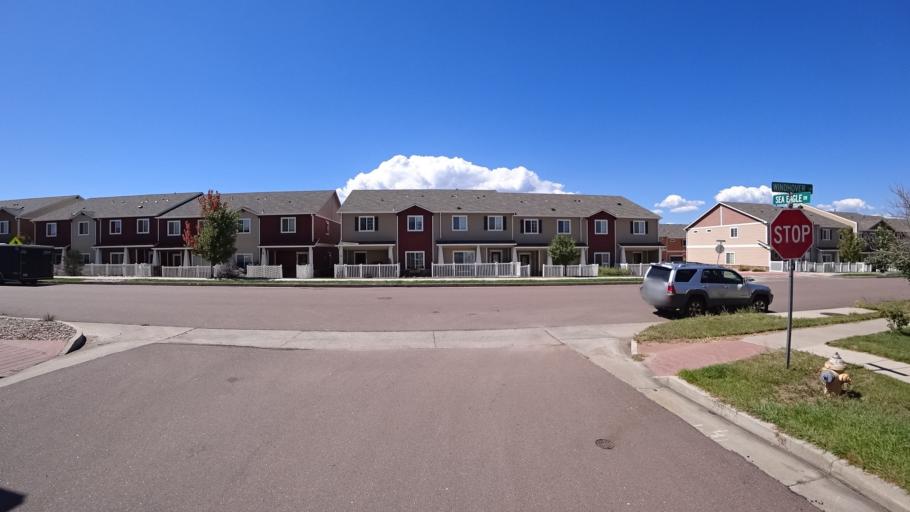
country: US
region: Colorado
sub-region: El Paso County
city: Stratmoor
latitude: 38.7873
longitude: -104.7362
